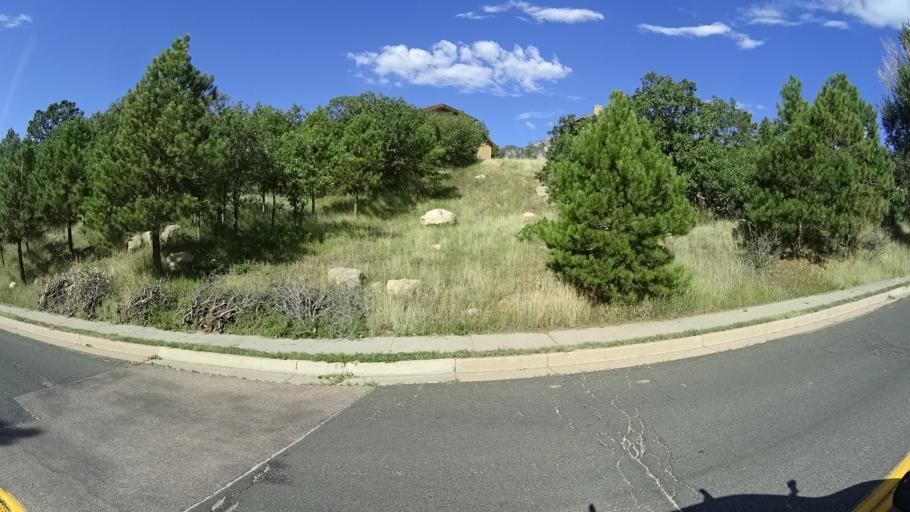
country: US
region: Colorado
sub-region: El Paso County
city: Fort Carson
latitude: 38.7594
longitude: -104.8270
